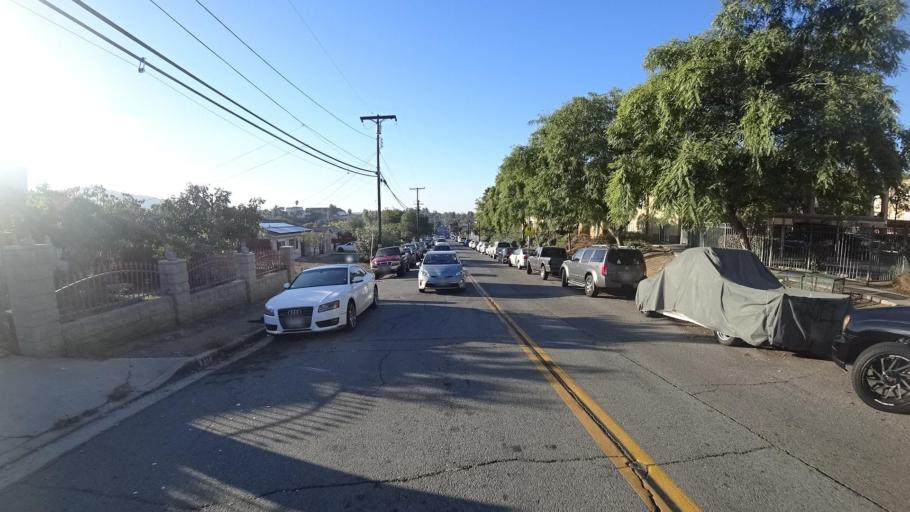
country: US
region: California
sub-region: San Diego County
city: La Presa
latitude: 32.7145
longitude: -117.0017
